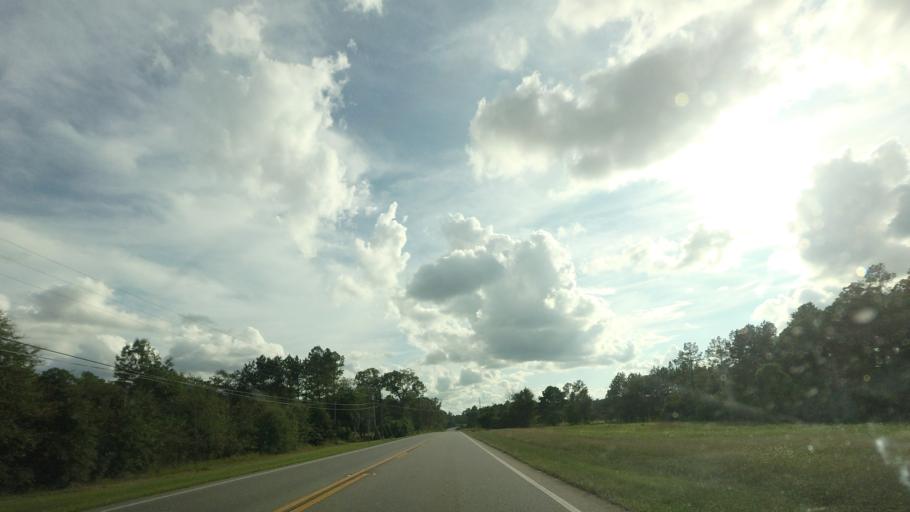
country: US
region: Georgia
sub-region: Pulaski County
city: Hawkinsville
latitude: 32.2994
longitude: -83.4297
